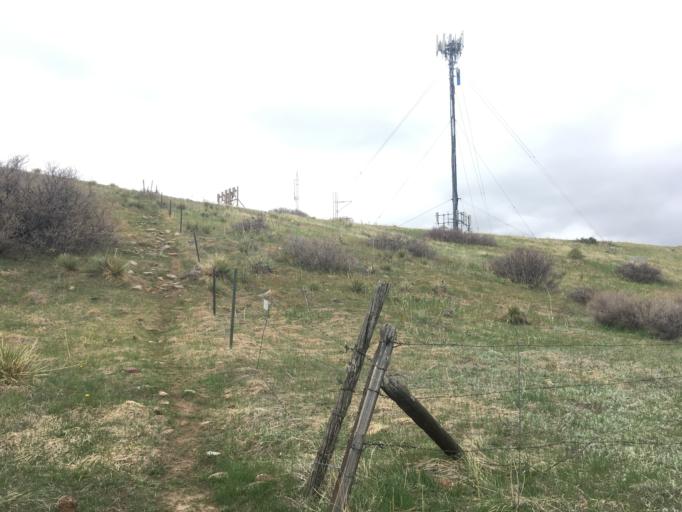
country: US
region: Colorado
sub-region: Boulder County
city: Superior
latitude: 39.9607
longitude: -105.2129
